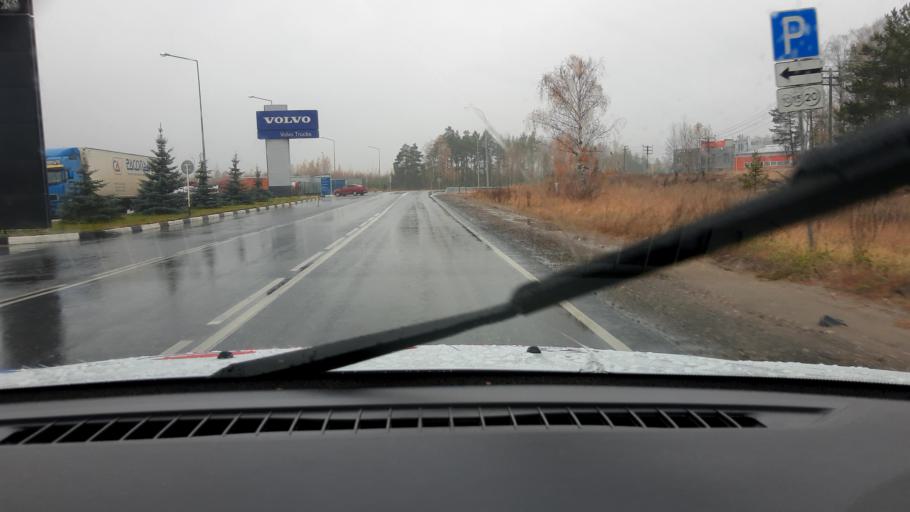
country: RU
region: Nizjnij Novgorod
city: Babino
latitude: 56.2997
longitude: 43.5943
